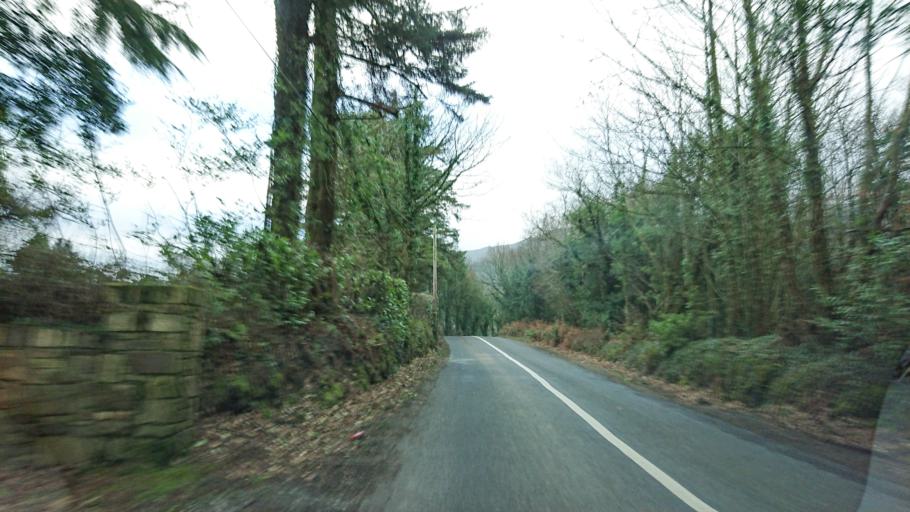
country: IE
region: Munster
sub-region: South Tipperary
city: Cluain Meala
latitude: 52.3204
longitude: -7.5787
